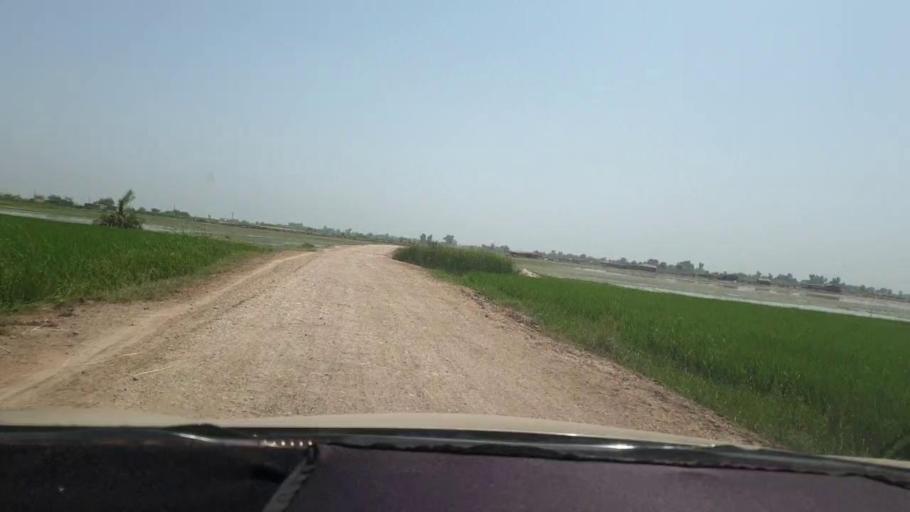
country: PK
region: Sindh
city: Shahdadkot
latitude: 27.8246
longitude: 67.9944
